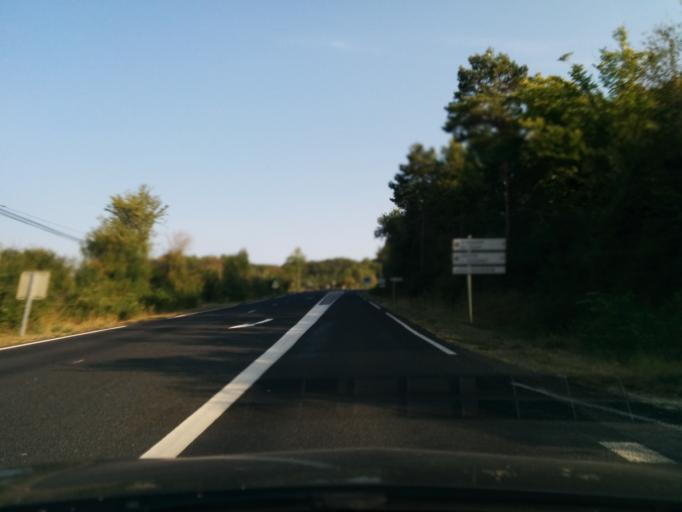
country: FR
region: Midi-Pyrenees
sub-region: Departement du Lot
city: Le Vigan
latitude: 44.7733
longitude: 1.4762
